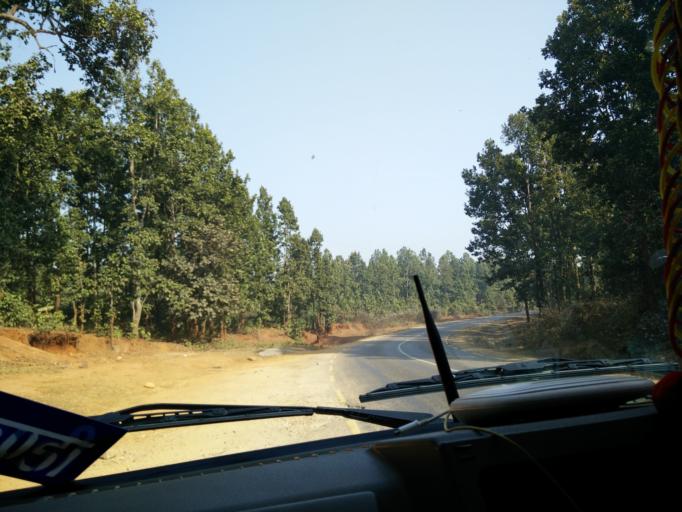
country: NP
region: Central Region
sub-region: Narayani Zone
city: Bharatpur
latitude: 27.6198
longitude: 84.0259
